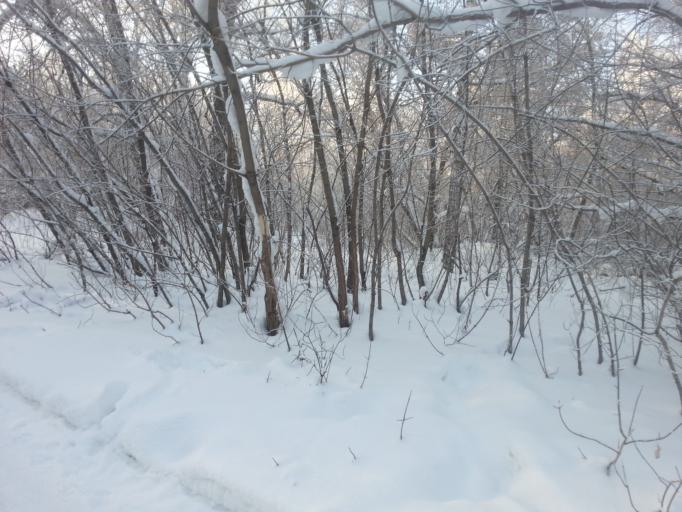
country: RU
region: Altai Krai
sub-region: Gorod Barnaulskiy
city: Barnaul
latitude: 53.3688
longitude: 83.7208
